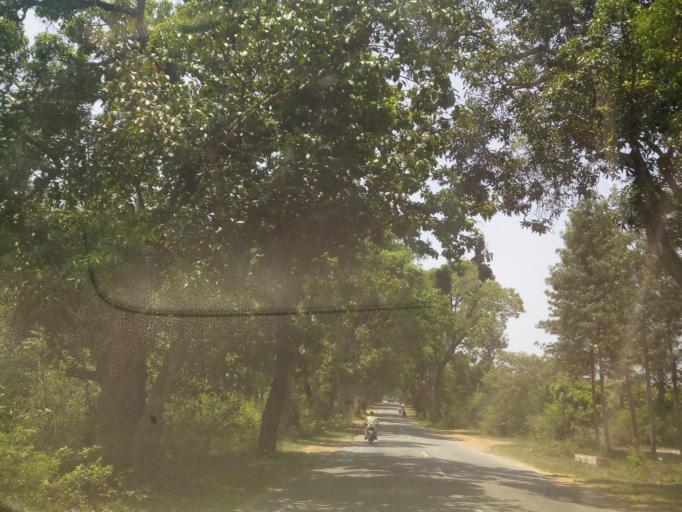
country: IN
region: Karnataka
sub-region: Hassan
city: Alur
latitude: 12.9549
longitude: 75.9118
